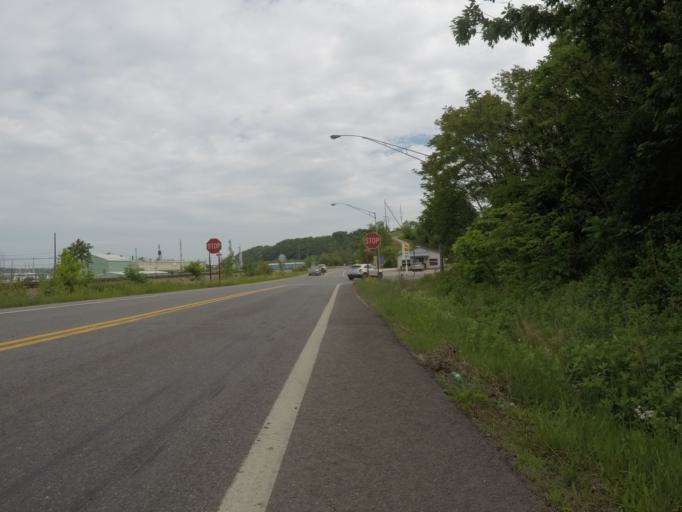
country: US
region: West Virginia
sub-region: Wayne County
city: Kenova
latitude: 38.3697
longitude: -82.5918
